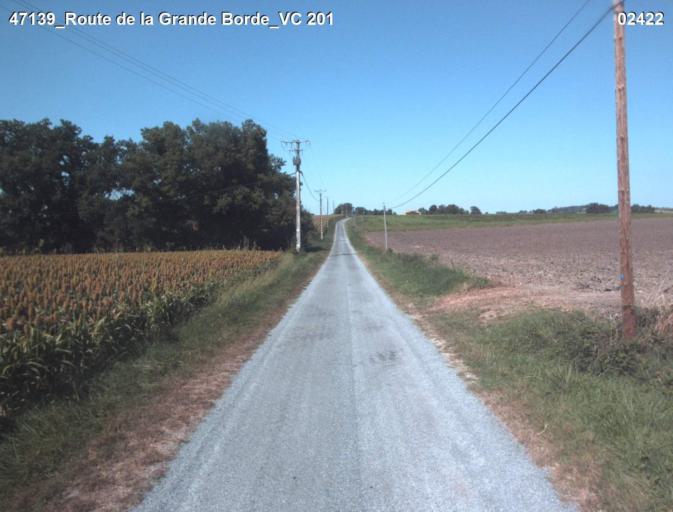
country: FR
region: Aquitaine
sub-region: Departement du Lot-et-Garonne
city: Nerac
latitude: 44.0807
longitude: 0.3811
